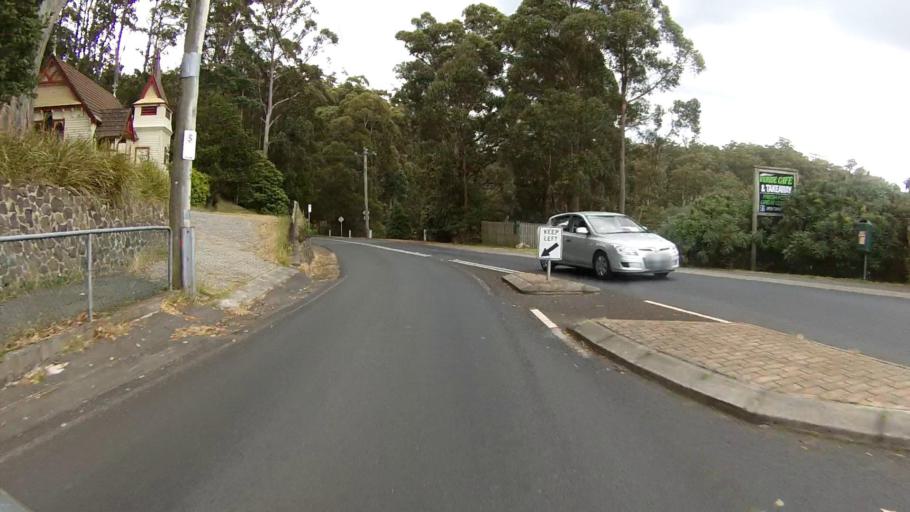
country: AU
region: Tasmania
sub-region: Hobart
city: Dynnyrne
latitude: -42.9221
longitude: 147.2600
